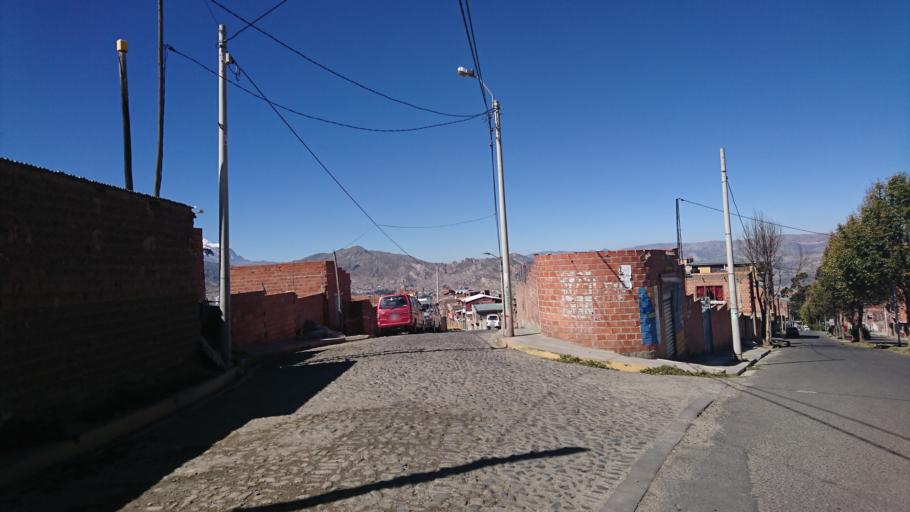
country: BO
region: La Paz
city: La Paz
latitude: -16.4925
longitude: -68.1024
